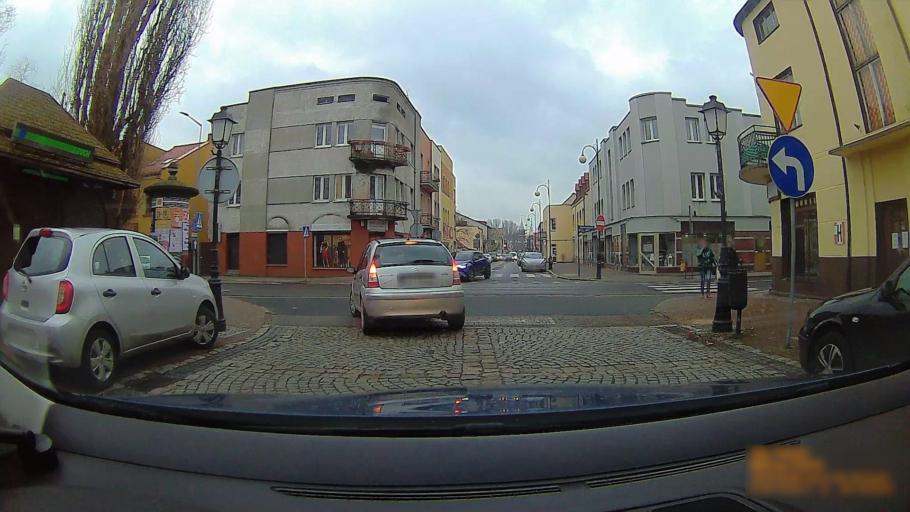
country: PL
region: Greater Poland Voivodeship
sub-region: Konin
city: Konin
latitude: 52.2089
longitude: 18.2545
